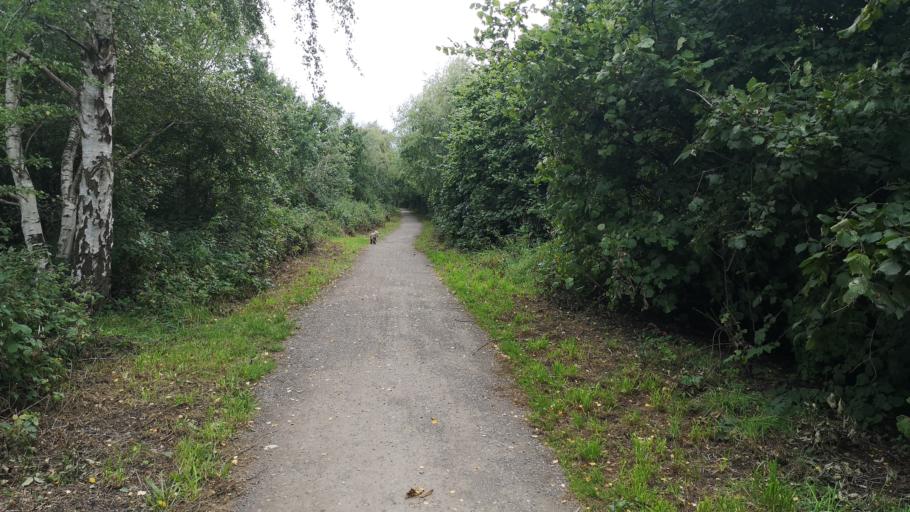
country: GB
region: England
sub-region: City and Borough of Wakefield
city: Notton
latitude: 53.6201
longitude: -1.4699
